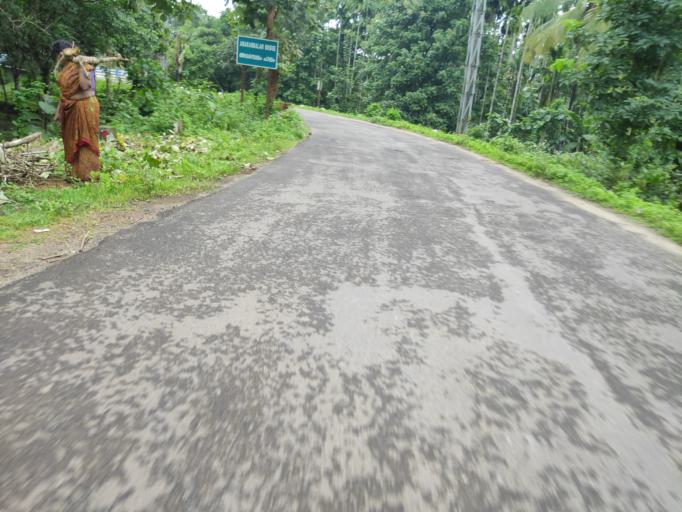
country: IN
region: Kerala
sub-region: Malappuram
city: Manjeri
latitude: 11.2303
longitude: 76.2754
